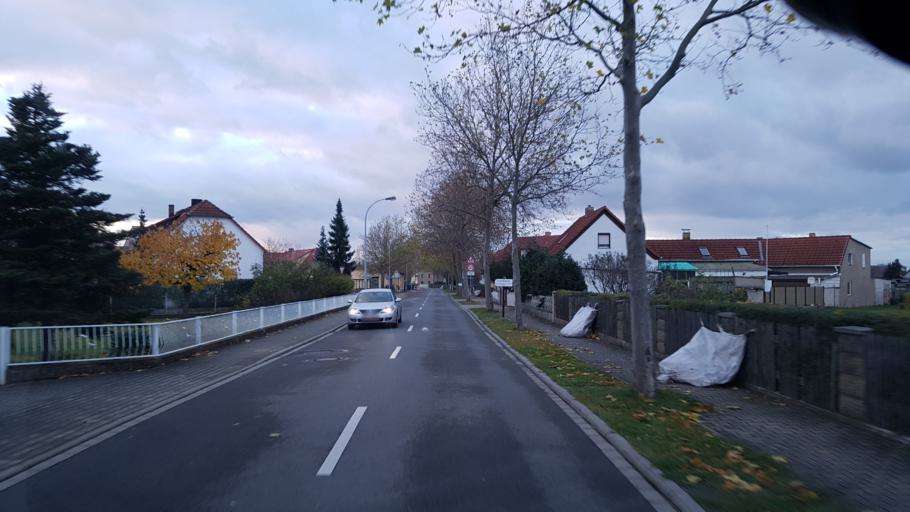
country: DE
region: Brandenburg
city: Tettau
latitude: 51.4295
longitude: 13.7334
